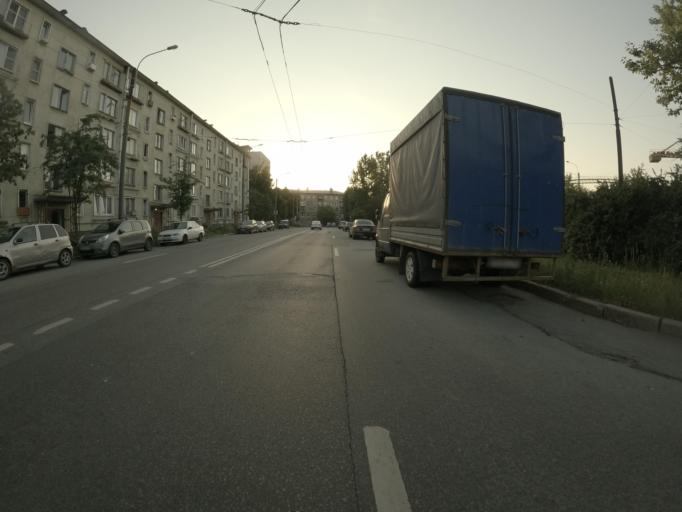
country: RU
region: St.-Petersburg
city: Avtovo
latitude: 59.8701
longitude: 30.2748
